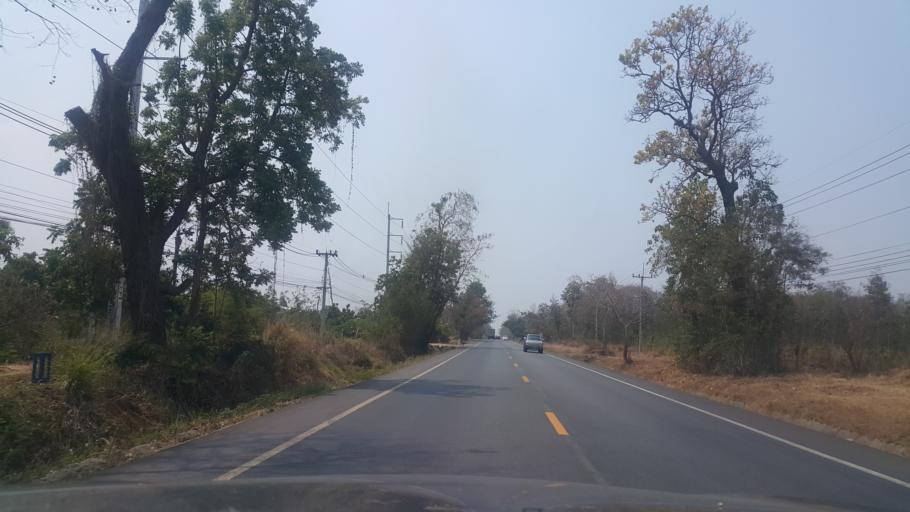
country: TH
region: Chiang Mai
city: Doi Lo
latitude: 18.4214
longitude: 98.8577
